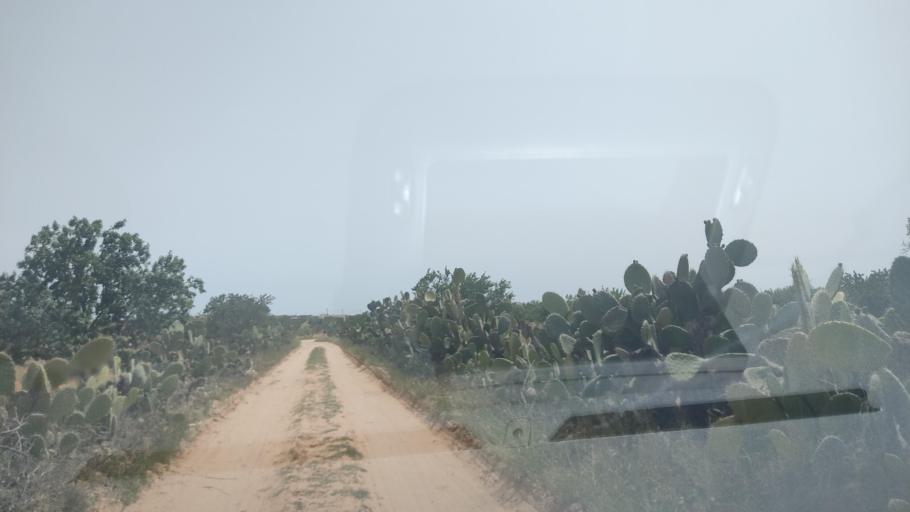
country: TN
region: Safaqis
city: Sfax
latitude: 34.8339
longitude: 10.6001
